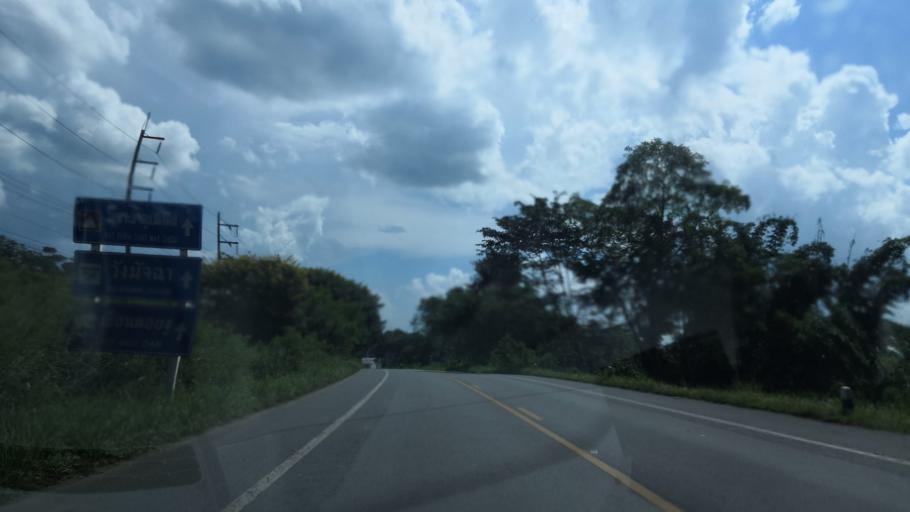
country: TH
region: Chiang Rai
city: Mae Suai
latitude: 19.5561
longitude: 99.4933
